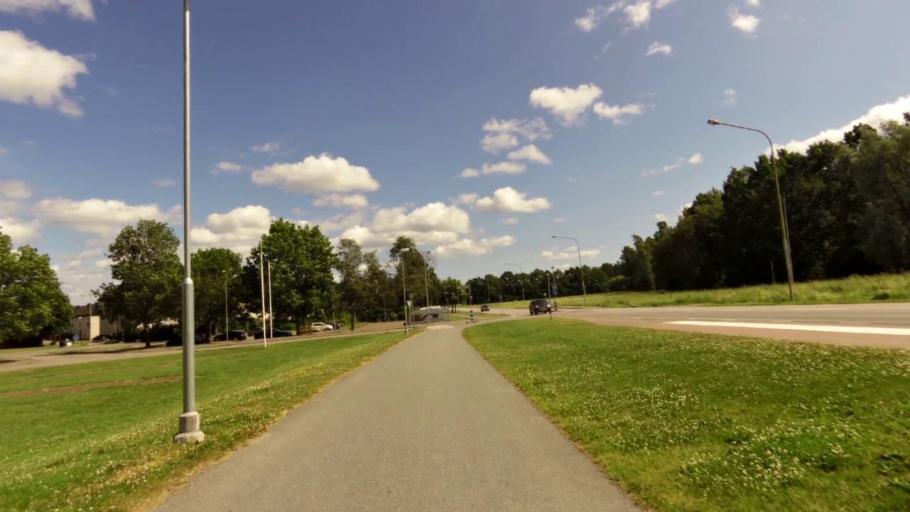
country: SE
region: OEstergoetland
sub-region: Linkopings Kommun
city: Linkoping
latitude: 58.4229
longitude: 15.5741
